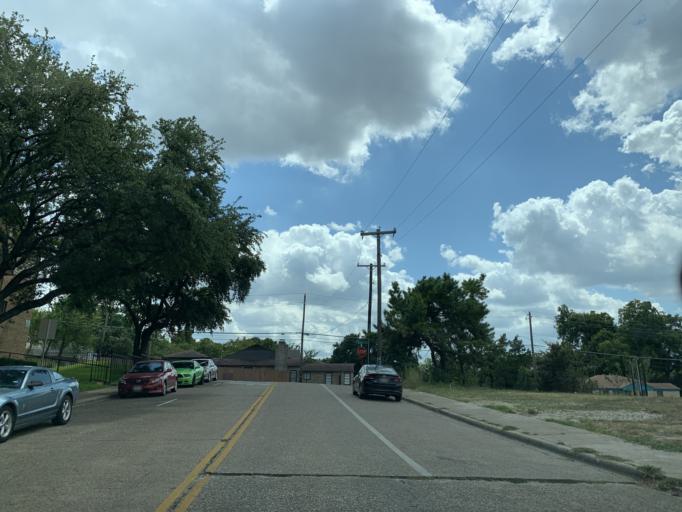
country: US
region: Texas
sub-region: Dallas County
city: Cockrell Hill
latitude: 32.7501
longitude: -96.8525
